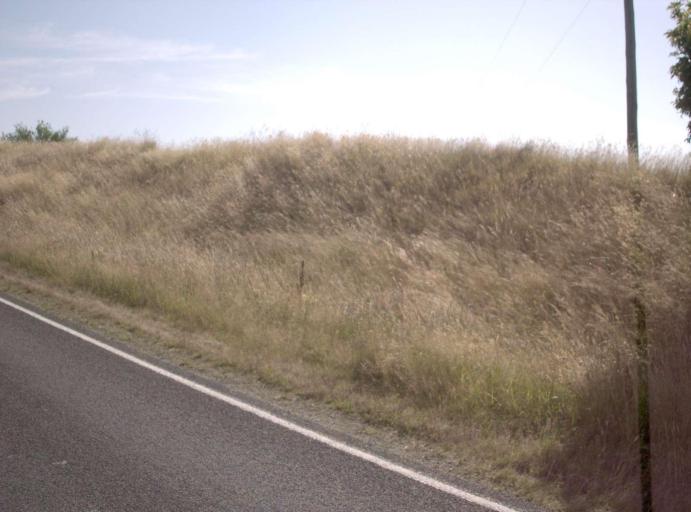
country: AU
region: Victoria
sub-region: Baw Baw
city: Warragul
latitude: -38.3201
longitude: 145.7697
